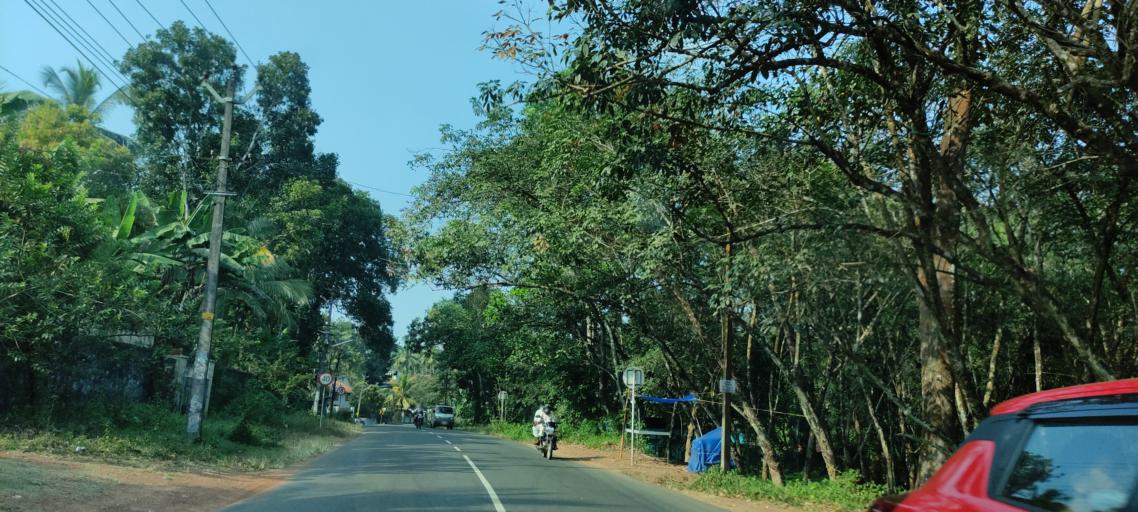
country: IN
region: Kerala
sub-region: Pattanamtitta
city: Adur
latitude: 9.1046
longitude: 76.6906
